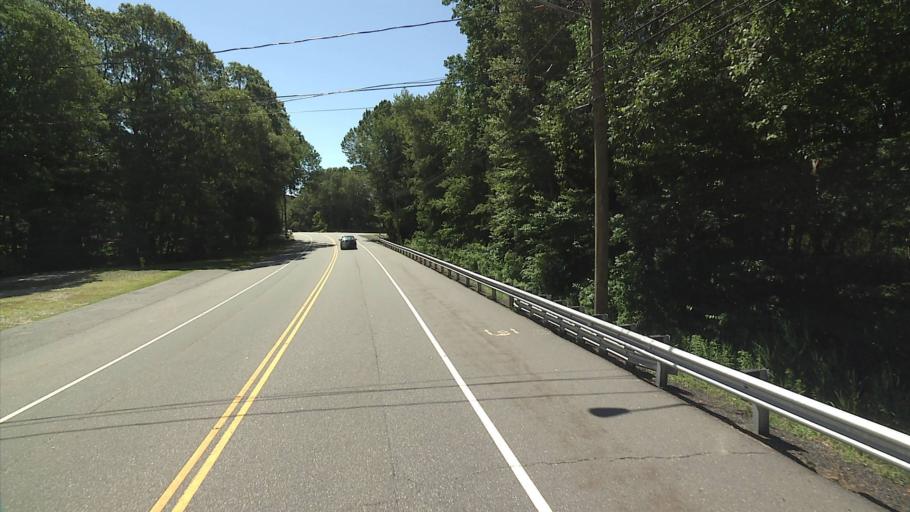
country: US
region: Connecticut
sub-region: New London County
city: Poquonock Bridge
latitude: 41.3388
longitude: -72.0075
